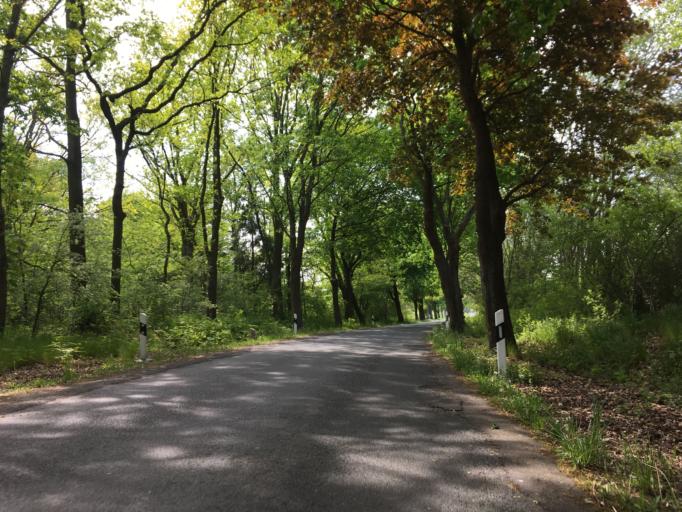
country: DE
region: Brandenburg
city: Melchow
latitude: 52.7468
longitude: 13.6851
